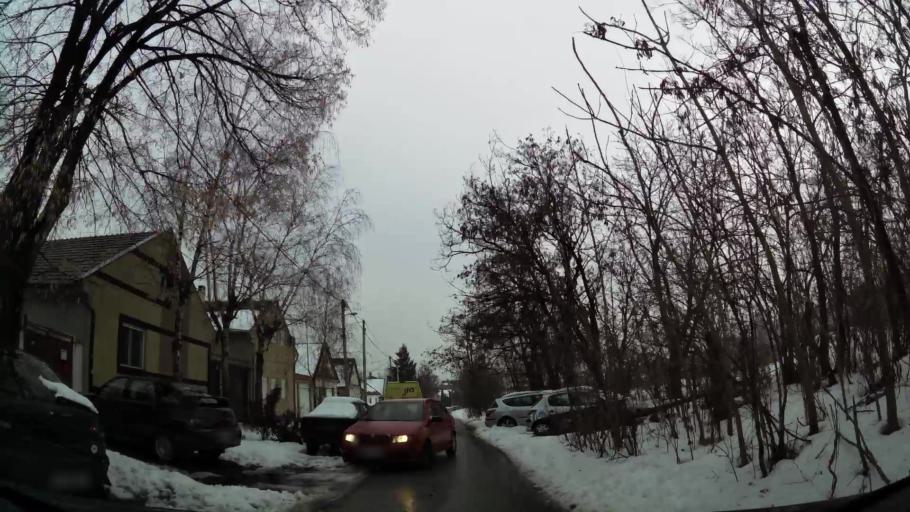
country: RS
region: Central Serbia
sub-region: Belgrade
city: Zemun
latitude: 44.8503
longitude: 20.3778
